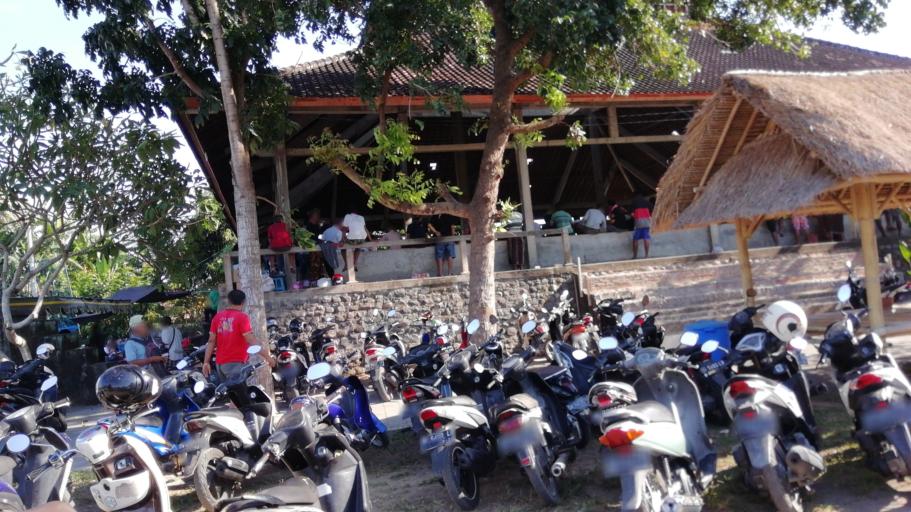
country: ID
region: Bali
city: Banjar Pasekan
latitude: -8.6095
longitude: 115.2892
